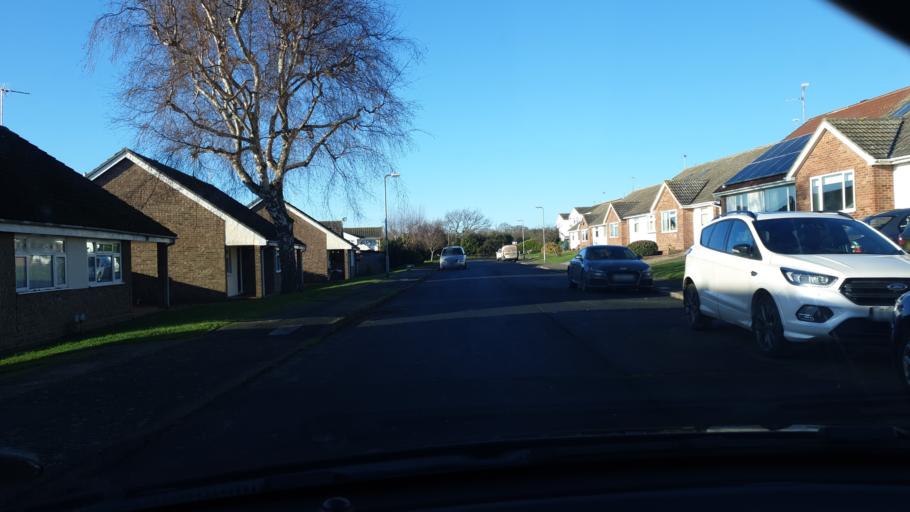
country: GB
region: England
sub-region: Essex
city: Brightlingsea
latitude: 51.8149
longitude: 1.0176
